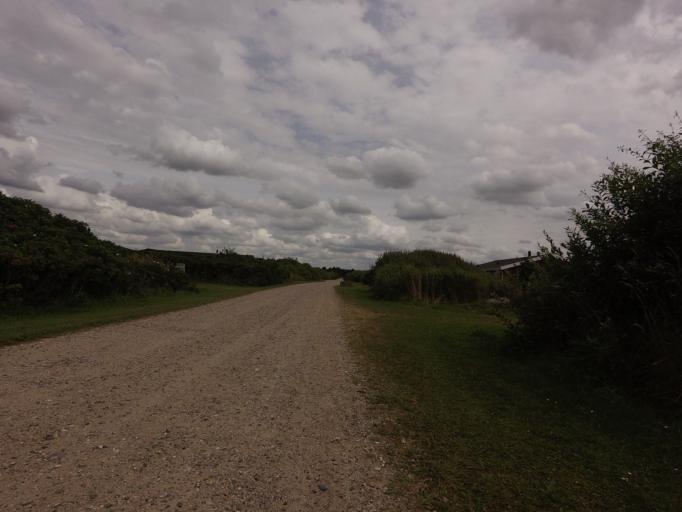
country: DK
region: North Denmark
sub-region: Jammerbugt Kommune
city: Pandrup
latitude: 57.3579
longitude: 9.6995
